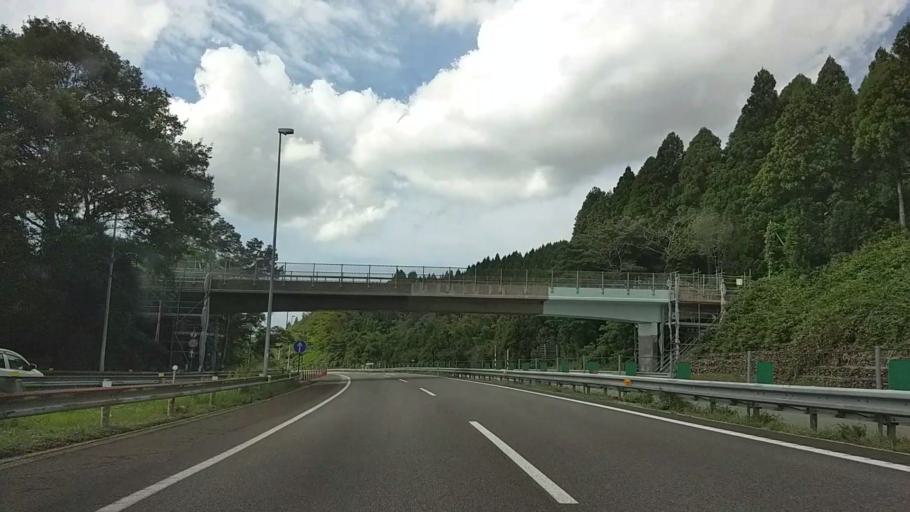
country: JP
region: Ishikawa
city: Tsubata
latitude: 36.6057
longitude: 136.7192
